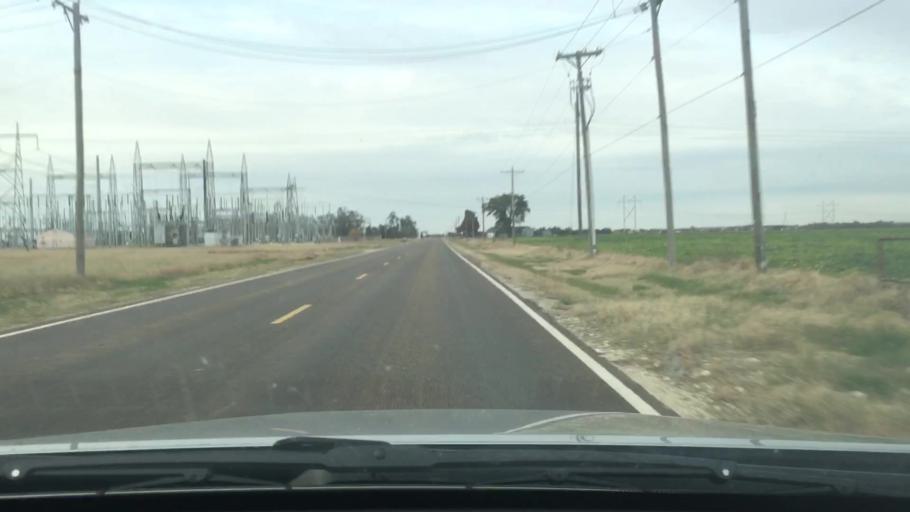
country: US
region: Kansas
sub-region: Sedgwick County
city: Colwich
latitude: 37.7905
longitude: -97.5182
